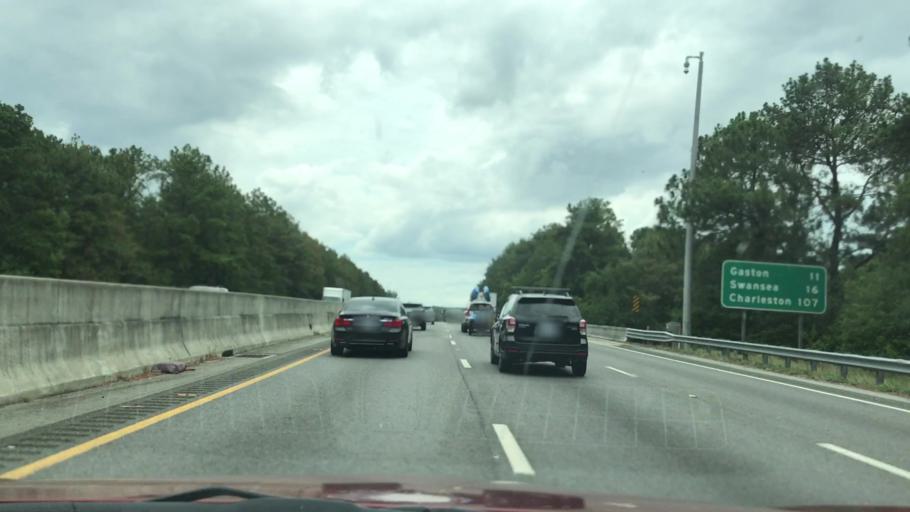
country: US
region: South Carolina
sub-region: Lexington County
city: Springdale
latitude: 33.9468
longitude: -81.0903
